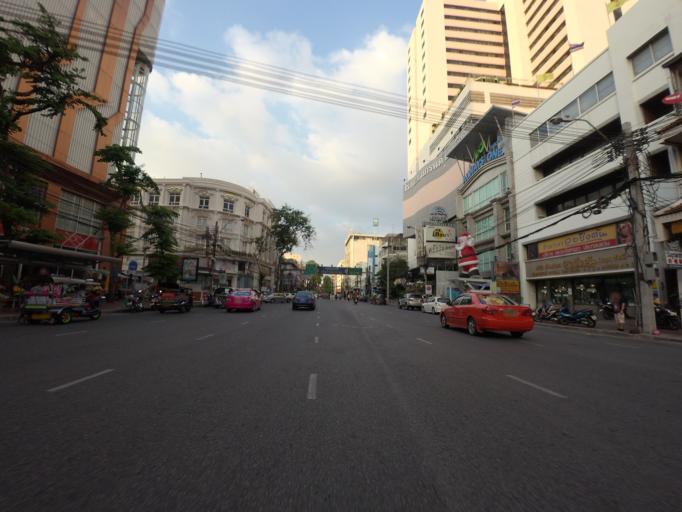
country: TH
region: Bangkok
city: Bangkok
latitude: 13.7454
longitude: 100.5027
